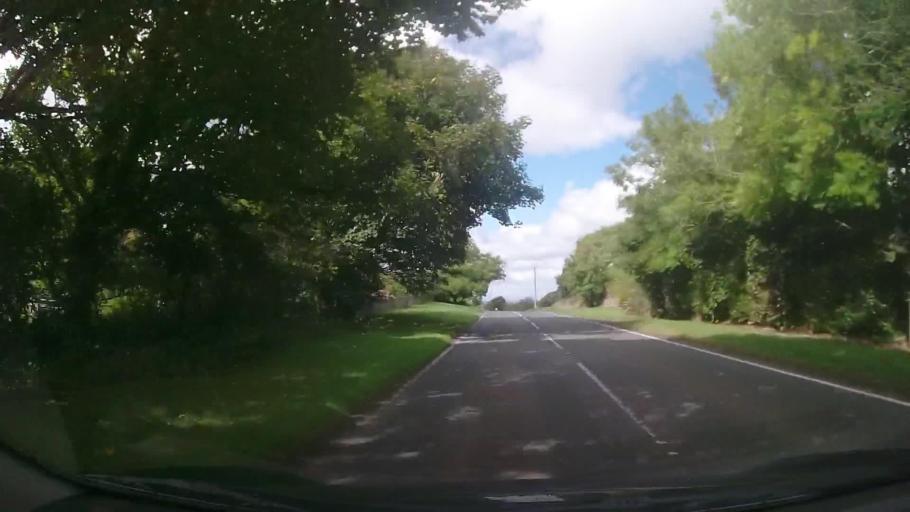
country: GB
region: Wales
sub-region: Pembrokeshire
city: Manorbier
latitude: 51.6524
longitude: -4.7884
